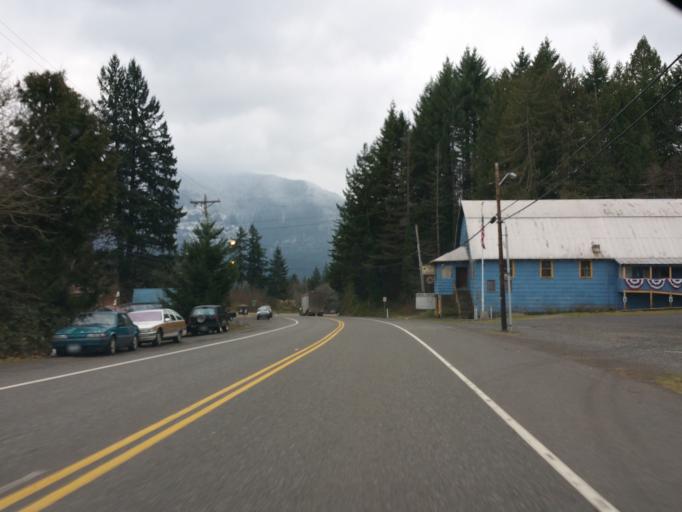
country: US
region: Washington
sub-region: Skamania County
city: Carson
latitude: 45.7244
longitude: -121.8205
